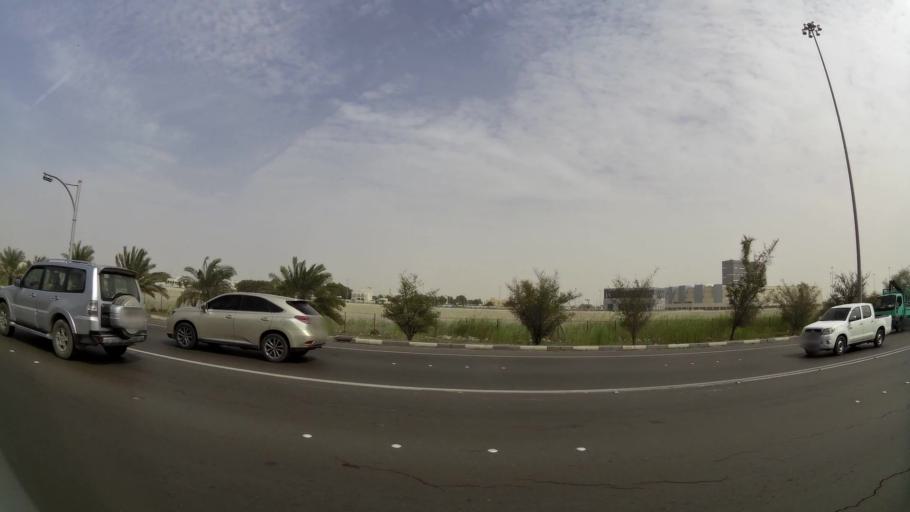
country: AE
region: Abu Dhabi
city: Abu Dhabi
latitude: 24.3792
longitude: 54.5248
